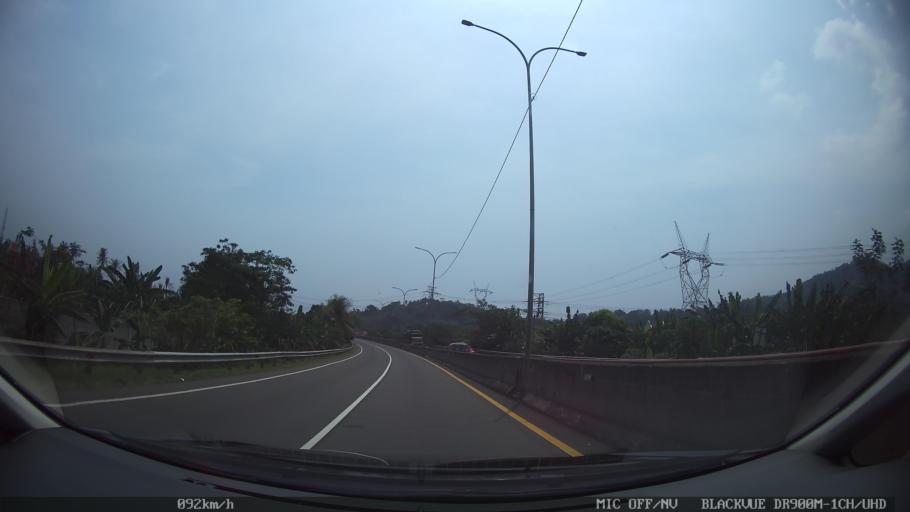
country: ID
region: Banten
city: Curug
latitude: -5.9821
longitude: 106.0298
